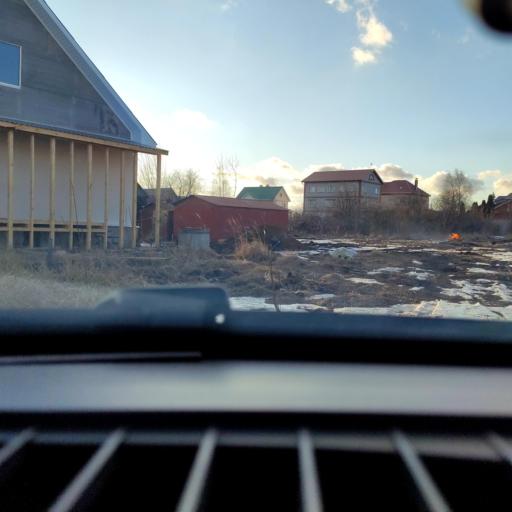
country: RU
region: Voronezj
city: Devitsa
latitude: 51.6355
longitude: 38.9266
